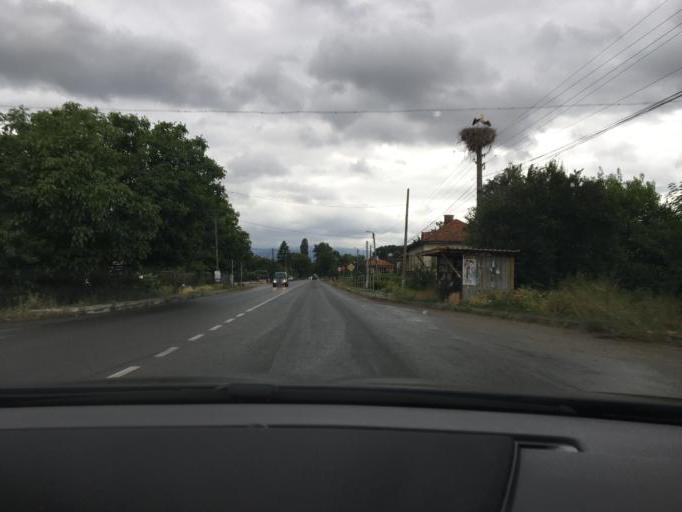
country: BG
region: Kyustendil
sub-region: Obshtina Kyustendil
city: Kyustendil
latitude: 42.2794
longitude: 22.7332
